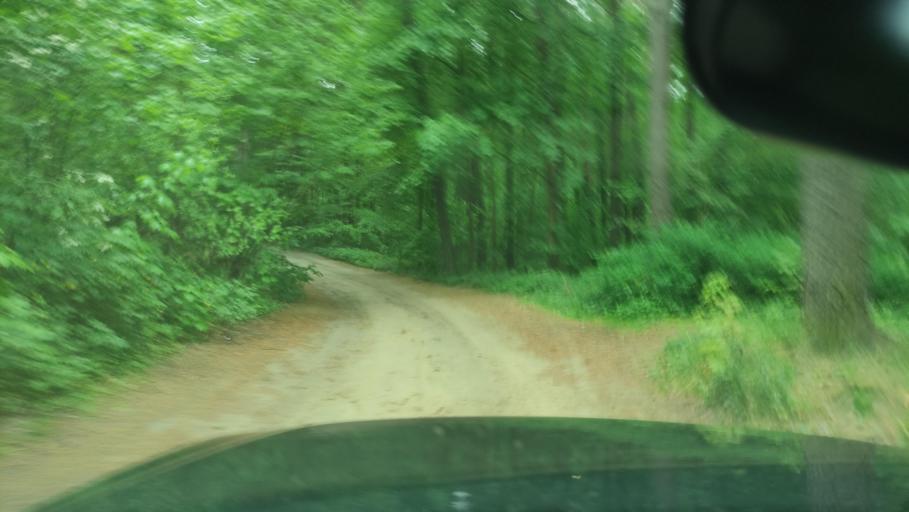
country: PL
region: Warmian-Masurian Voivodeship
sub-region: Powiat olsztynski
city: Olsztyn
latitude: 53.7589
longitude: 20.5206
